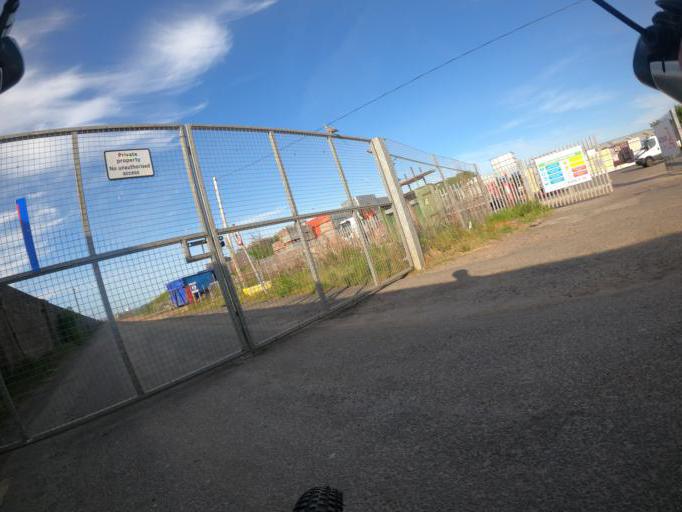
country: GB
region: Scotland
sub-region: Edinburgh
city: Edinburgh
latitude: 55.9841
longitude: -3.2335
